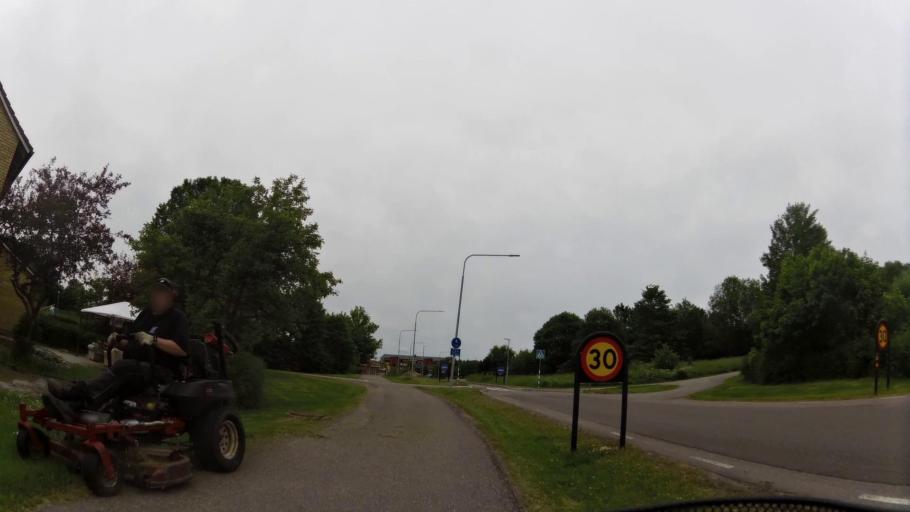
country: SE
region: OEstergoetland
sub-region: Linkopings Kommun
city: Linkoping
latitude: 58.3845
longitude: 15.5725
